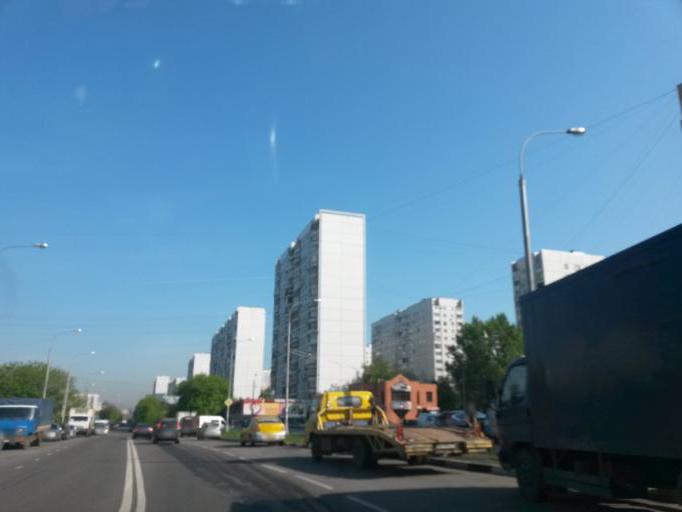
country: RU
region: Moscow
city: Brateyevo
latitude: 55.6344
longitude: 37.7646
